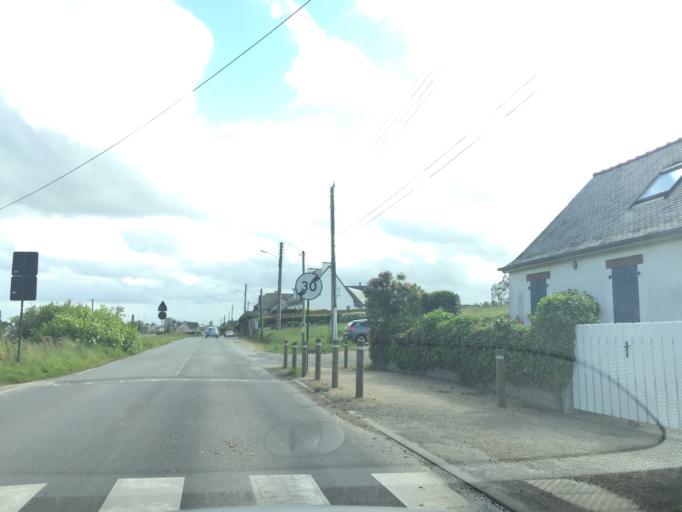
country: FR
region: Brittany
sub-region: Departement des Cotes-d'Armor
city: Lancieux
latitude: 48.6138
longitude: -2.1441
